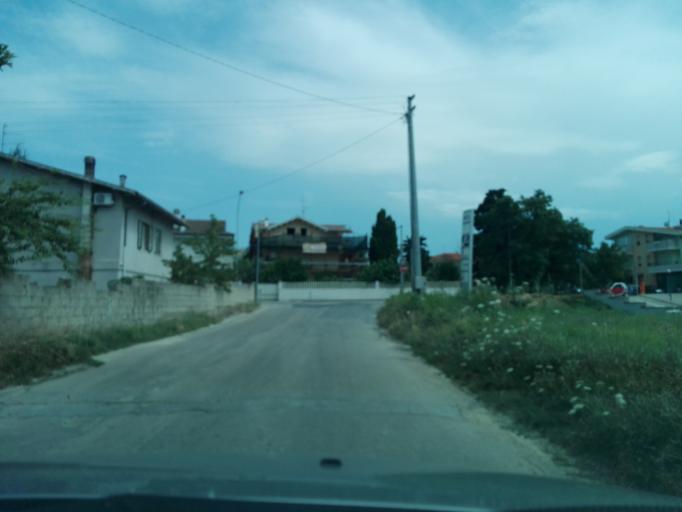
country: IT
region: Abruzzo
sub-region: Provincia di Pescara
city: Cappelle sul Tavo
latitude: 42.4834
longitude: 14.1161
